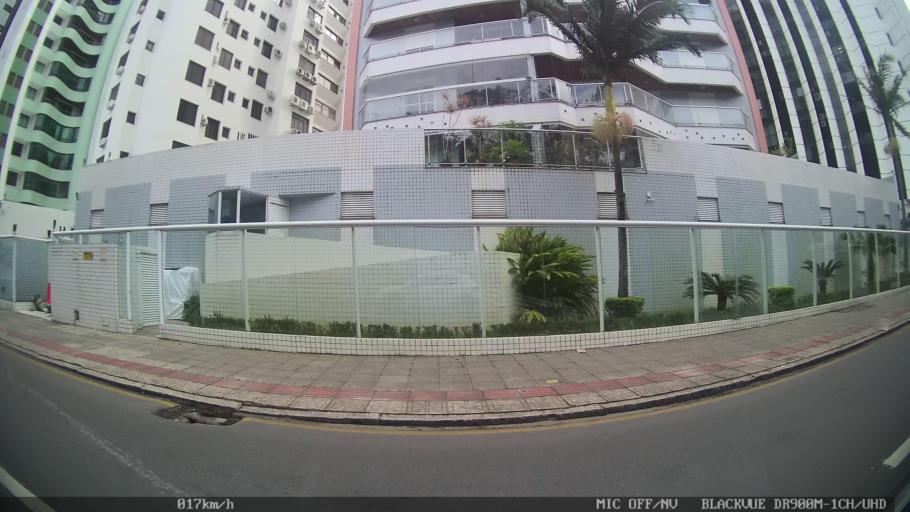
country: BR
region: Santa Catarina
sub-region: Florianopolis
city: Morro da Cruz
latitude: -27.5773
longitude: -48.5424
